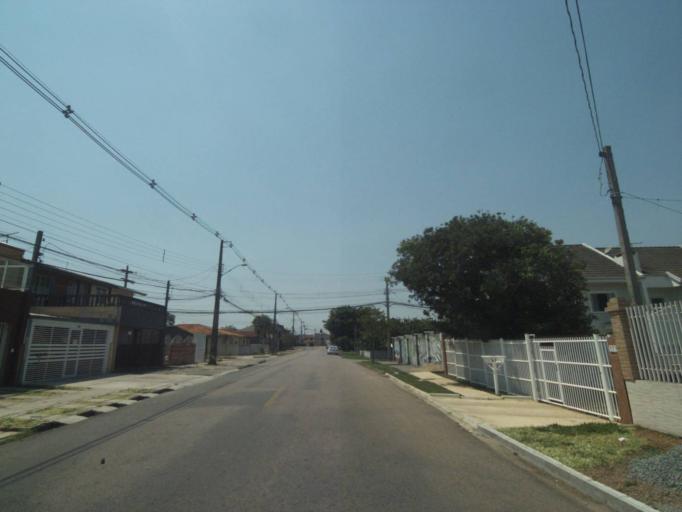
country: BR
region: Parana
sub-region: Sao Jose Dos Pinhais
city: Sao Jose dos Pinhais
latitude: -25.5102
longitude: -49.2647
